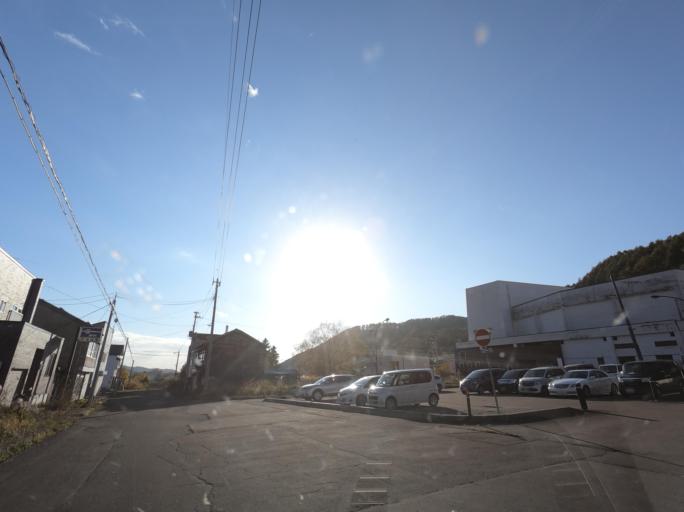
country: JP
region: Hokkaido
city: Iwamizawa
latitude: 43.0560
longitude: 141.9740
